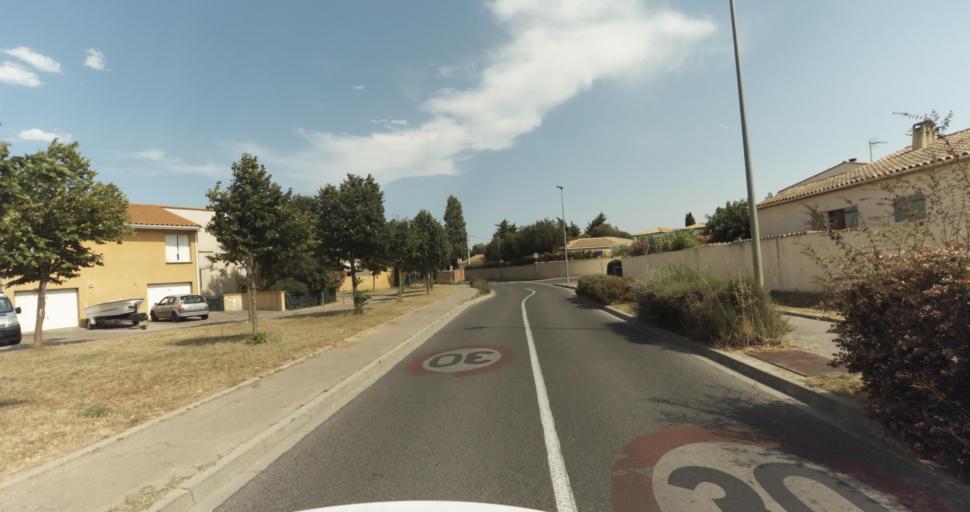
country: FR
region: Languedoc-Roussillon
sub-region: Departement des Pyrenees-Orientales
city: Alenya
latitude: 42.6428
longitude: 2.9768
